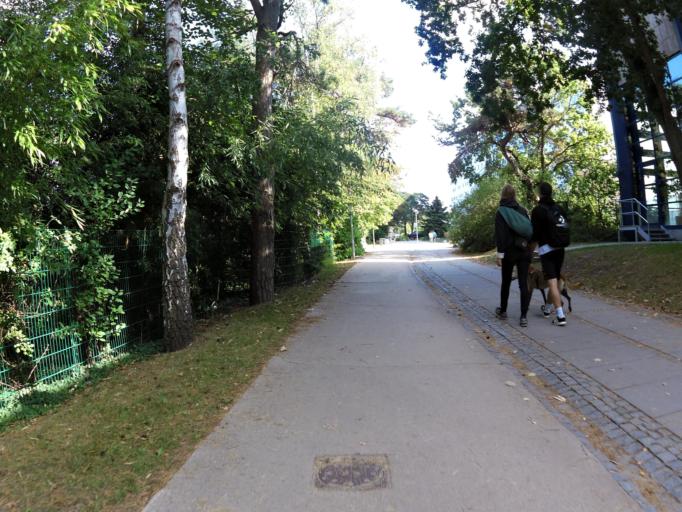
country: DE
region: Mecklenburg-Vorpommern
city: Ostseebad Zinnowitz
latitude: 54.0840
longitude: 13.9073
